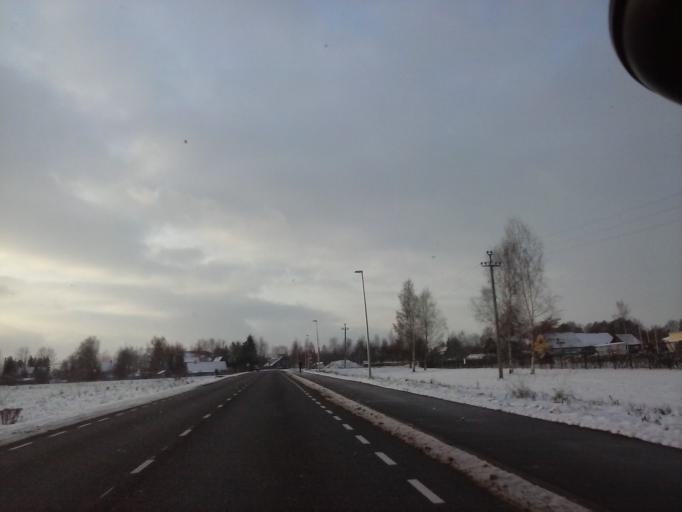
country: EE
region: Tartu
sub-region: UElenurme vald
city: Ulenurme
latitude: 58.3312
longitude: 26.7237
